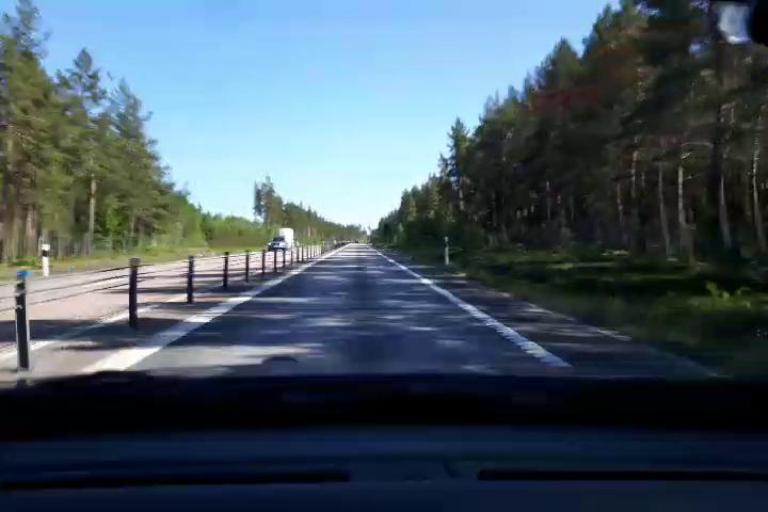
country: SE
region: Gaevleborg
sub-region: Gavle Kommun
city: Norrsundet
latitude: 60.9920
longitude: 17.0027
